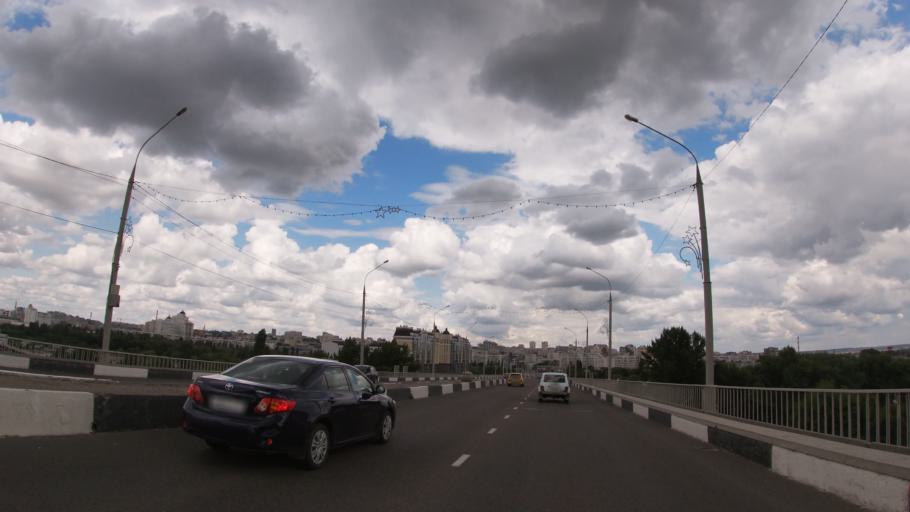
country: RU
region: Belgorod
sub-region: Belgorodskiy Rayon
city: Belgorod
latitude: 50.5853
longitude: 36.5866
